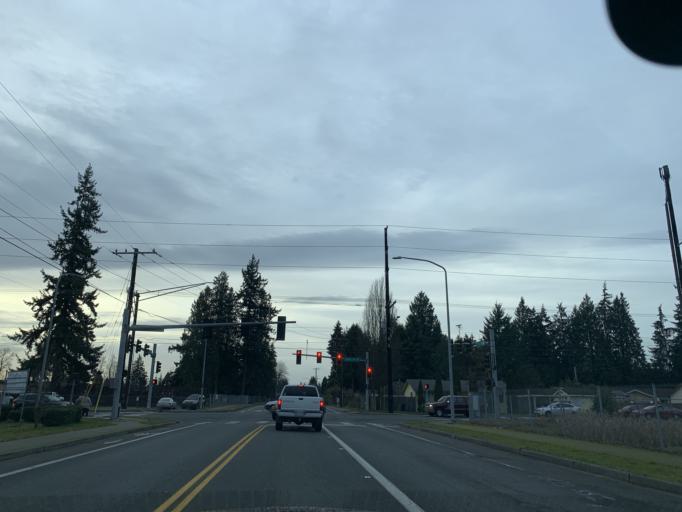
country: US
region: Washington
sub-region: Snohomish County
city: Marysville
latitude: 48.0862
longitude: -122.1622
